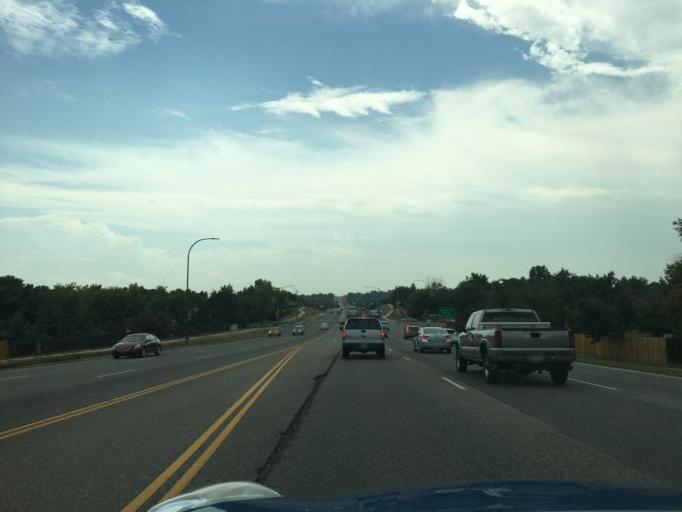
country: US
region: Colorado
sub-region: Adams County
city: Westminster
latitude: 39.8492
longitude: -105.0818
